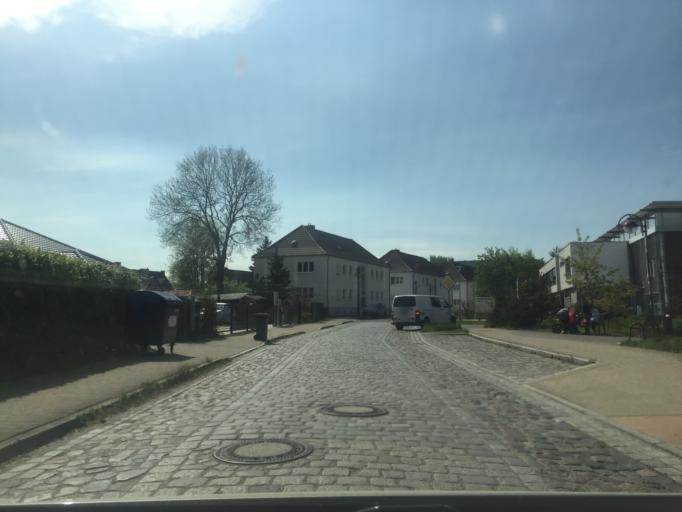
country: DE
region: Mecklenburg-Vorpommern
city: Torgelow
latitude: 53.6295
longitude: 14.0072
